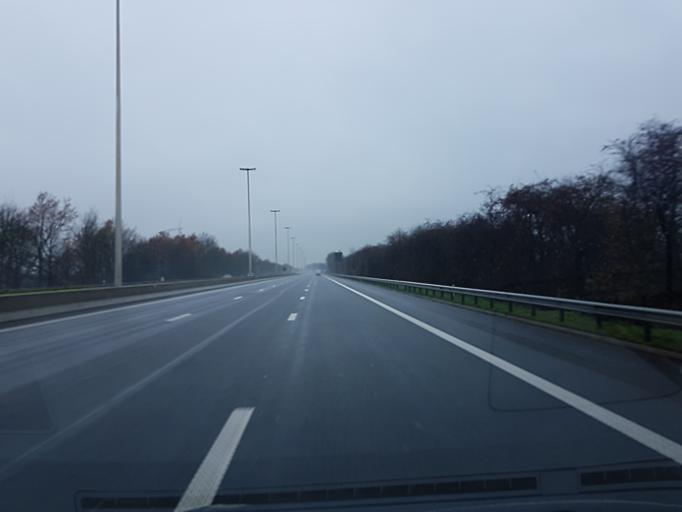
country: BE
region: Wallonia
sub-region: Province de Liege
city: Villers-le-Bouillet
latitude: 50.5899
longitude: 5.2528
